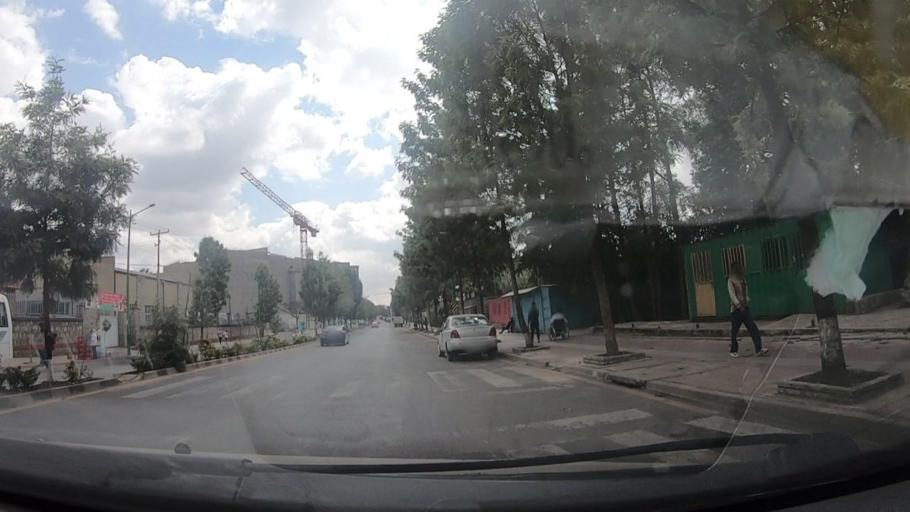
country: ET
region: Adis Abeba
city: Addis Ababa
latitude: 9.0024
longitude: 38.7357
